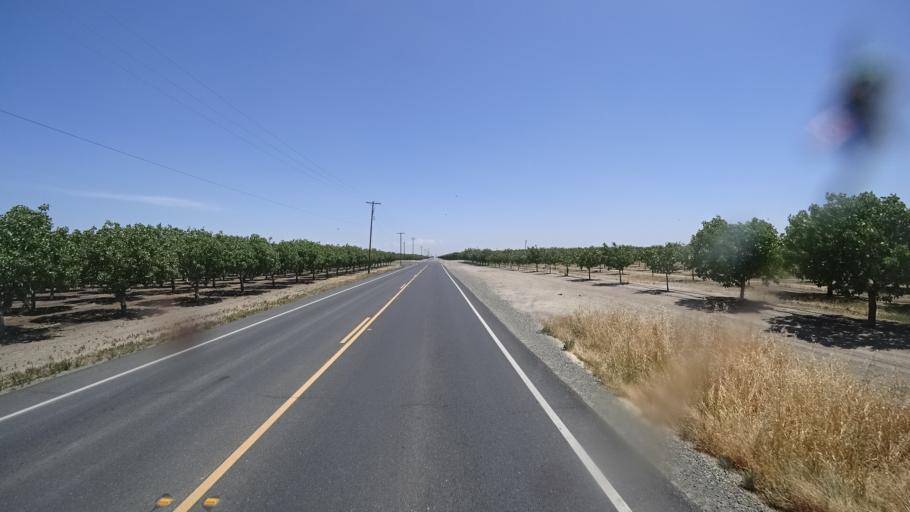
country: US
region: California
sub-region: Kings County
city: Corcoran
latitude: 36.0980
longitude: -119.5385
